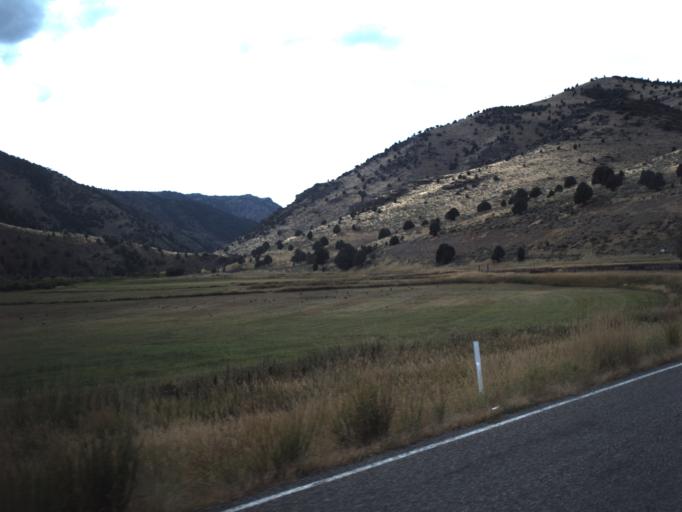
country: US
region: Utah
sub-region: Cache County
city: Millville
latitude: 41.6051
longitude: -111.5789
